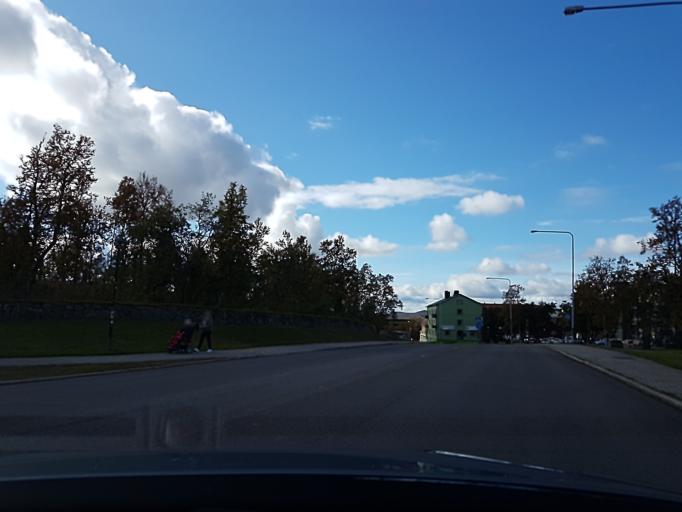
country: SE
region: Norrbotten
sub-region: Kiruna Kommun
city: Kiruna
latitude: 67.8529
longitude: 20.2333
